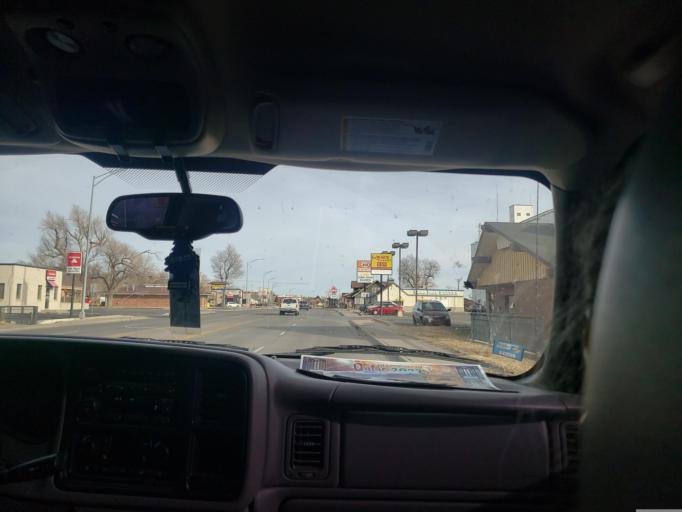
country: US
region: Kansas
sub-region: Ford County
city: Dodge City
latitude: 37.7533
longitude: -100.0279
